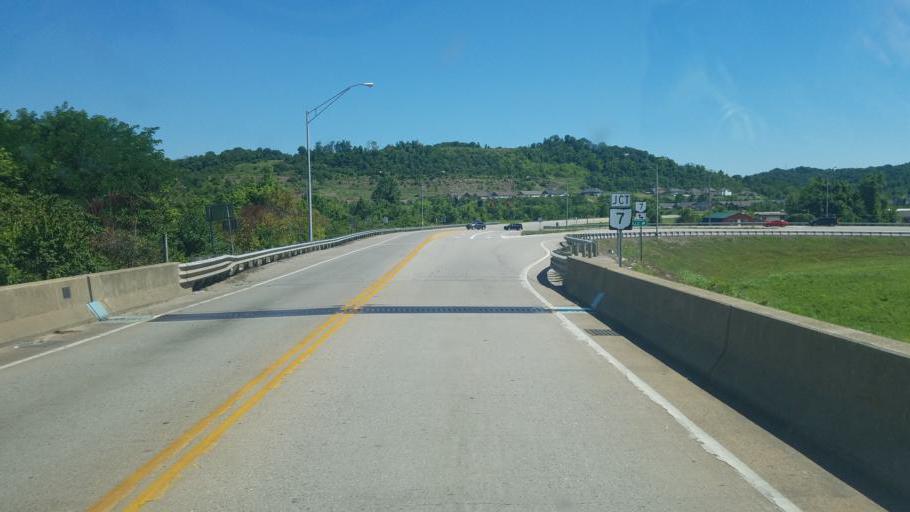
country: US
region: West Virginia
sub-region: Cabell County
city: Huntington
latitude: 38.4393
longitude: -82.3885
